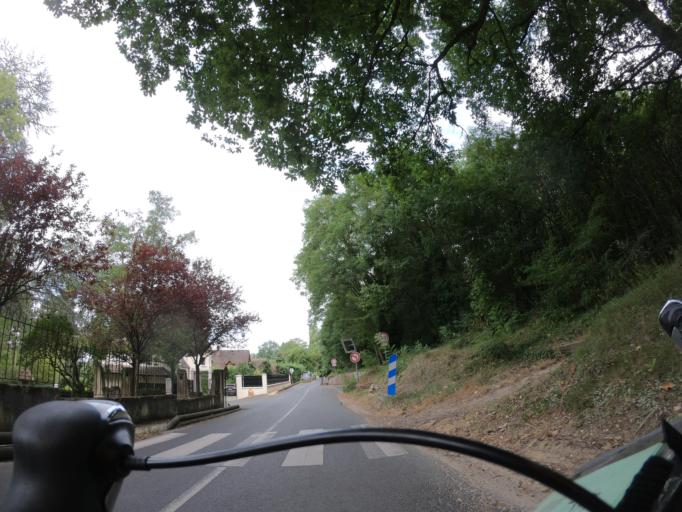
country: FR
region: Ile-de-France
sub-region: Departement de l'Essonne
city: Igny
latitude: 48.7435
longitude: 2.2345
